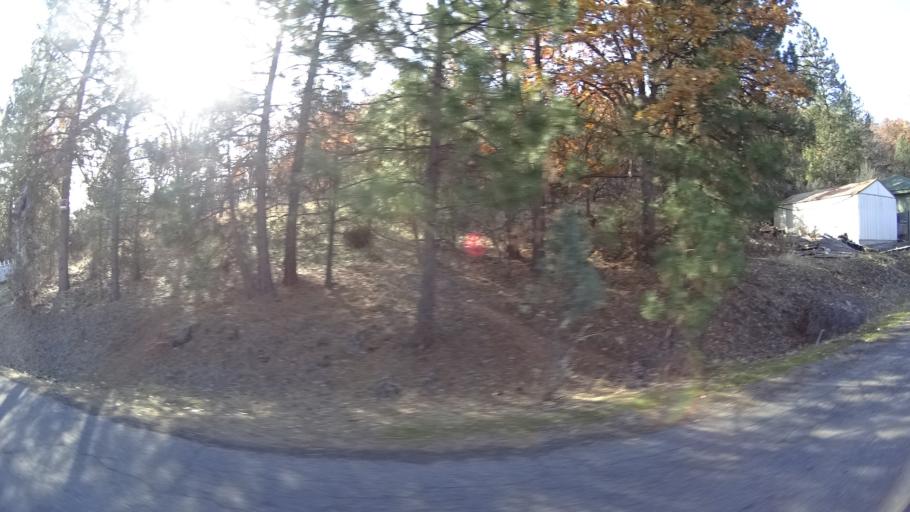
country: US
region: California
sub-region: Siskiyou County
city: Yreka
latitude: 41.7143
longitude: -122.6444
